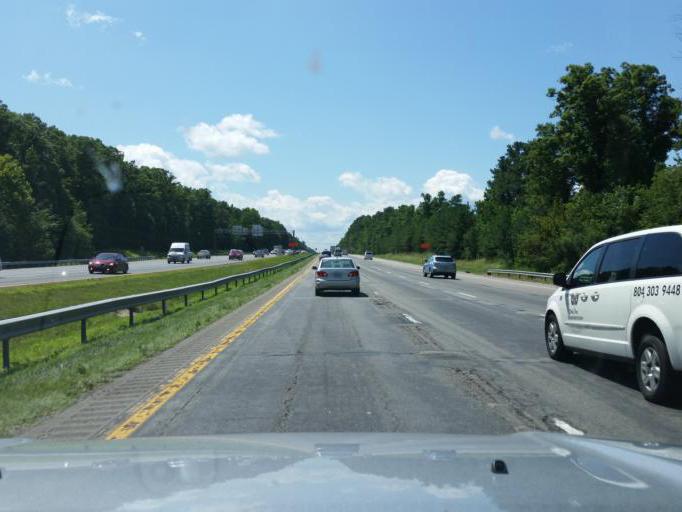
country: US
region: Virginia
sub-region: Hanover County
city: Ashland
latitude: 37.7571
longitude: -77.4589
